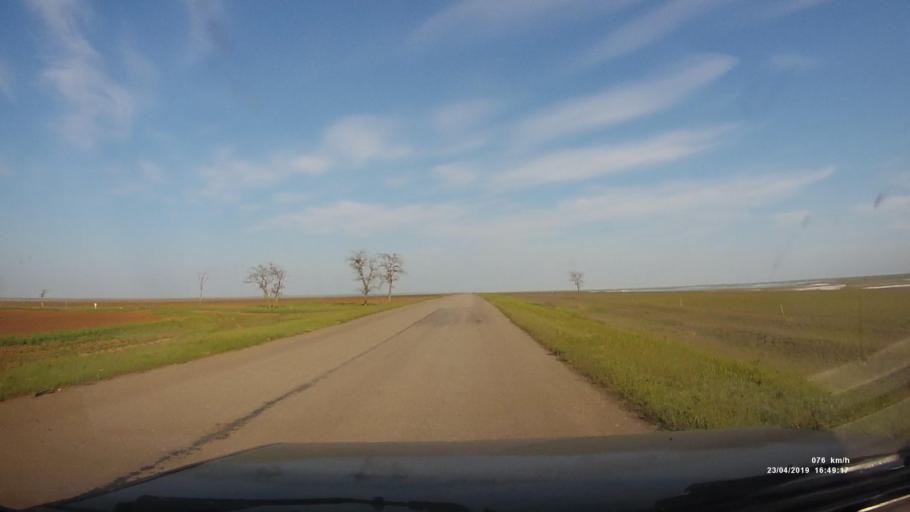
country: RU
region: Kalmykiya
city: Priyutnoye
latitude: 46.3316
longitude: 43.2744
